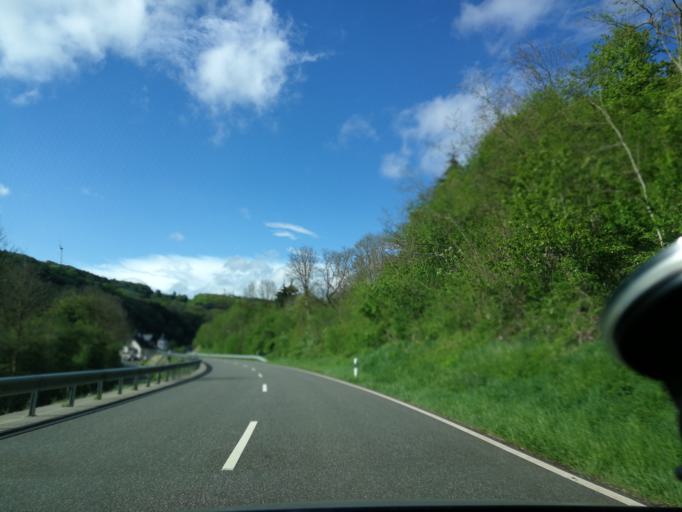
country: DE
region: Rheinland-Pfalz
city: Oberbillig
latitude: 49.7452
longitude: 6.5044
